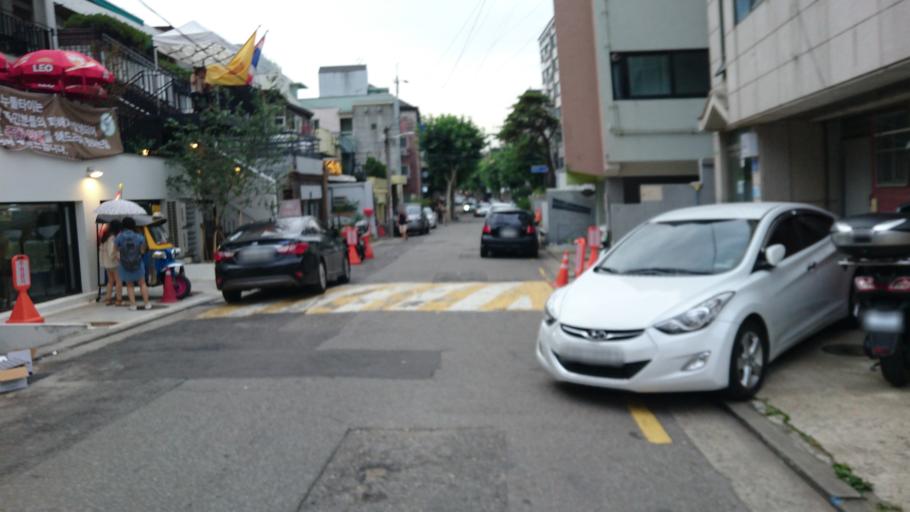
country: KR
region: Seoul
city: Seoul
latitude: 37.5652
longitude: 126.9238
